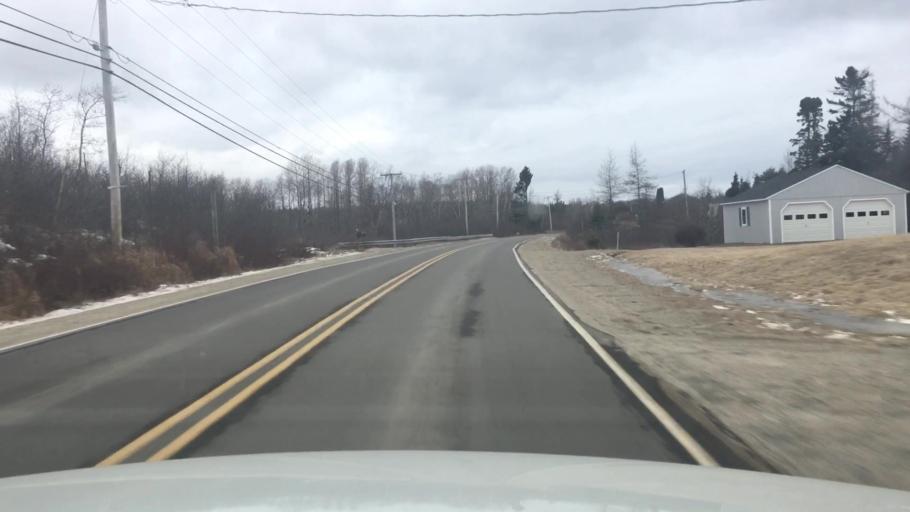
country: US
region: Maine
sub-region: Washington County
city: Jonesport
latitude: 44.5524
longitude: -67.6238
